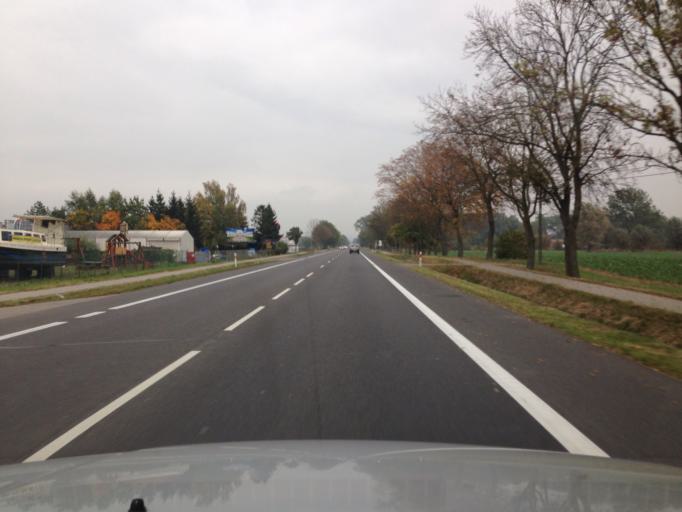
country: PL
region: Warmian-Masurian Voivodeship
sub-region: Powiat elblaski
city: Elblag
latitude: 54.1666
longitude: 19.3353
